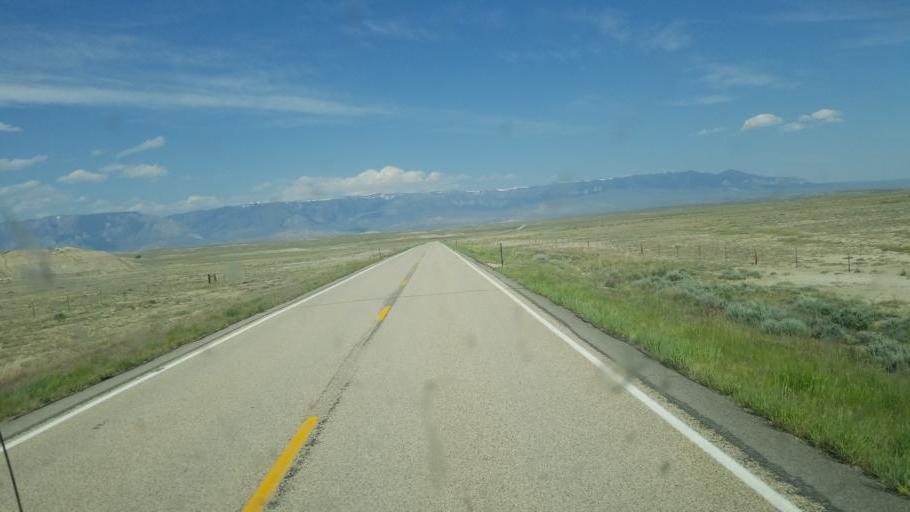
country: US
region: Wyoming
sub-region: Park County
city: Powell
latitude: 44.8453
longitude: -108.9988
